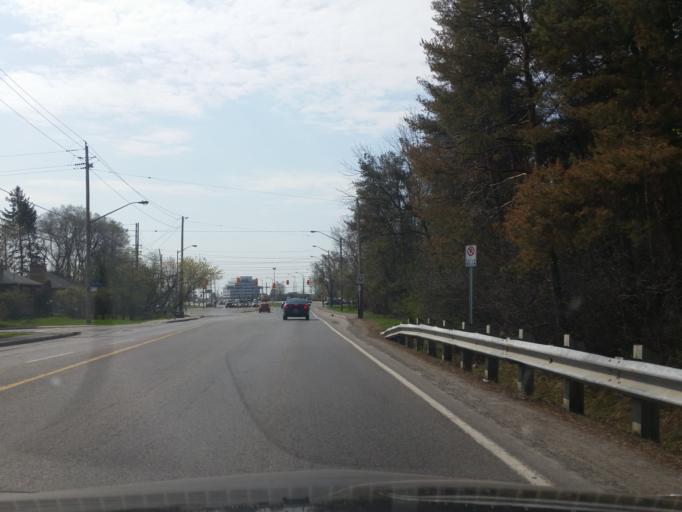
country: CA
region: Ontario
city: Ottawa
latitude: 45.4367
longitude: -75.6099
